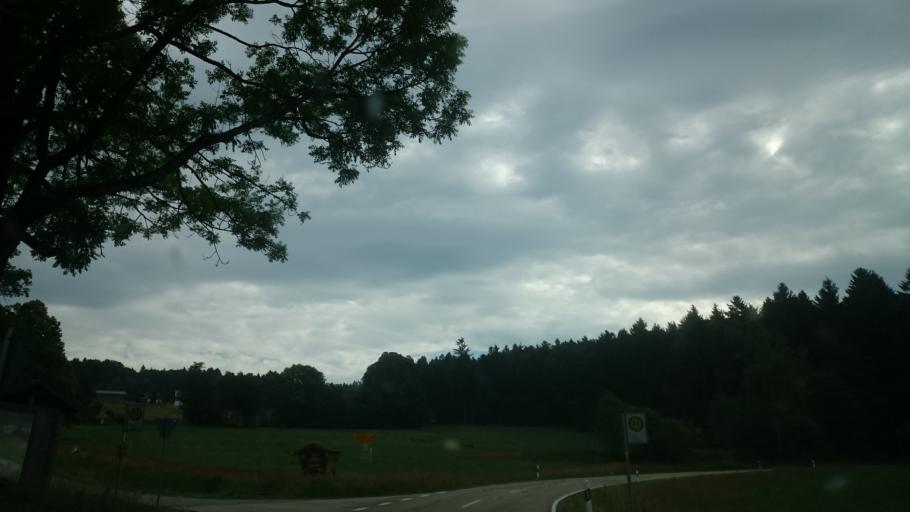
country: DE
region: Bavaria
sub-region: Lower Bavaria
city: Haibach
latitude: 49.0374
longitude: 12.7514
